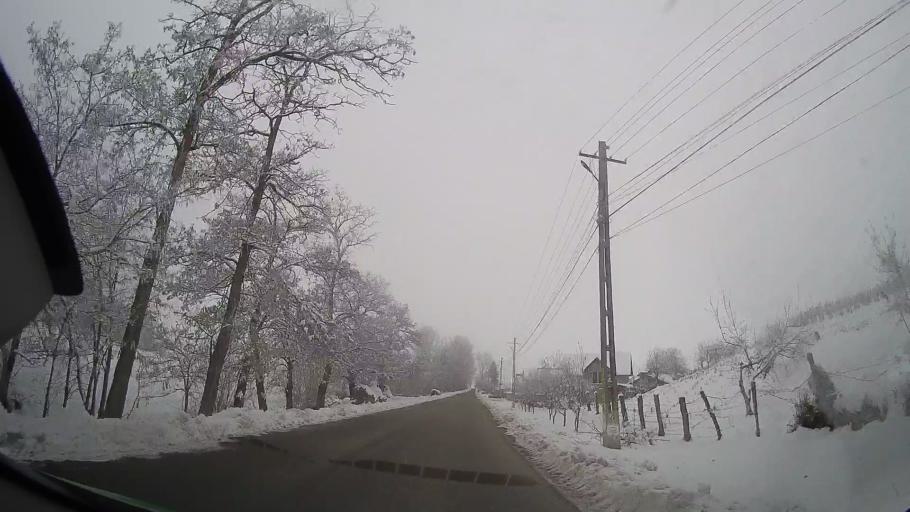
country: RO
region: Neamt
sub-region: Comuna Valea Ursului
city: Chilii
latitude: 46.8490
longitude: 27.0433
